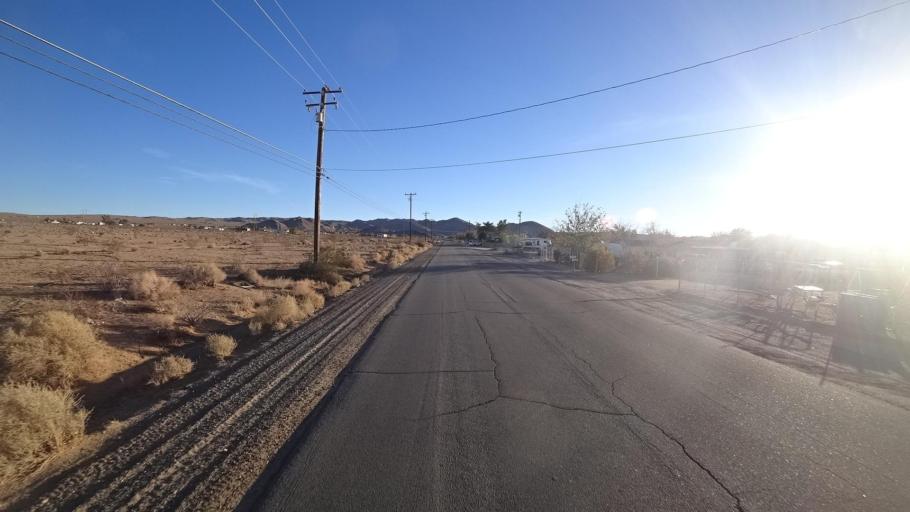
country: US
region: California
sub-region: Kern County
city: Ridgecrest
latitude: 35.5960
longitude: -117.6528
